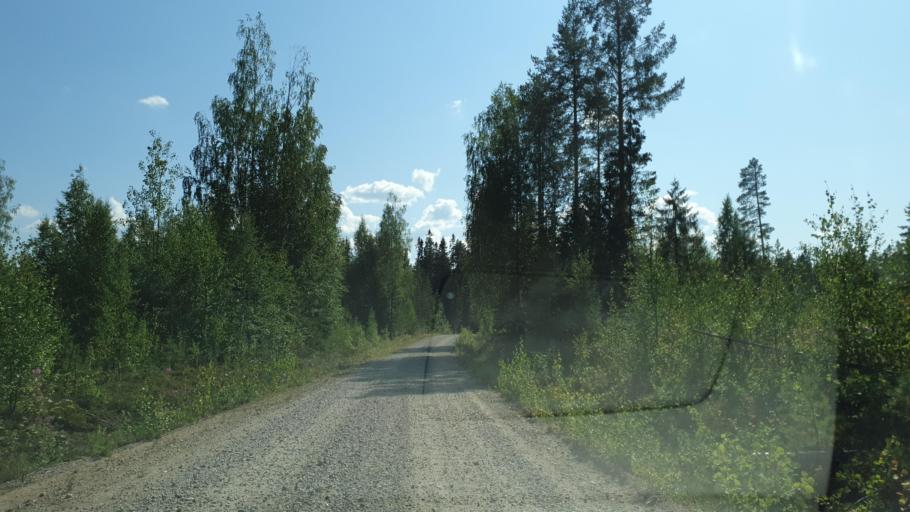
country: FI
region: Kainuu
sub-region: Kehys-Kainuu
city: Kuhmo
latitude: 63.9796
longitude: 29.5440
